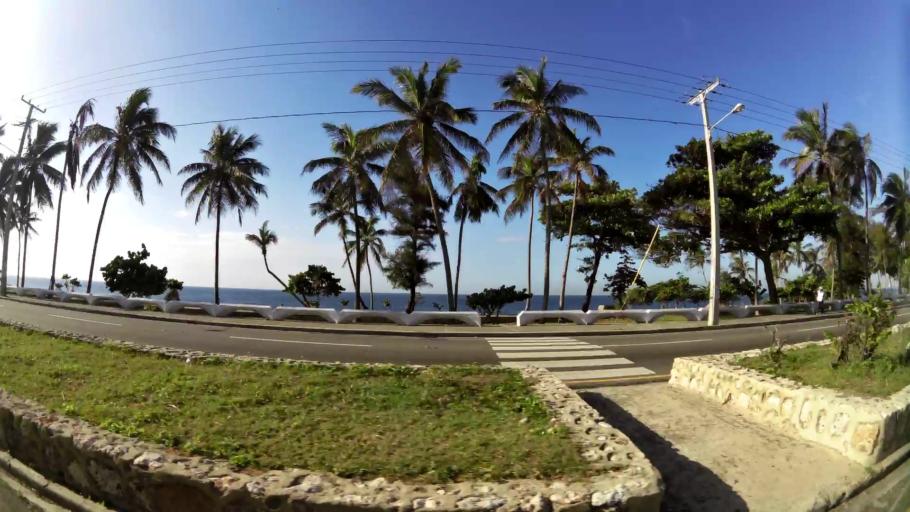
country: DO
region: Santo Domingo
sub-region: Santo Domingo
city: Santo Domingo Este
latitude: 18.4689
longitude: -69.8538
